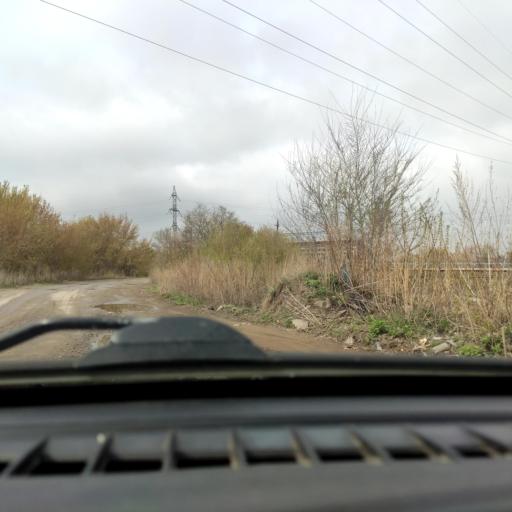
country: RU
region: Samara
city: Zhigulevsk
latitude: 53.5392
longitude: 49.4962
